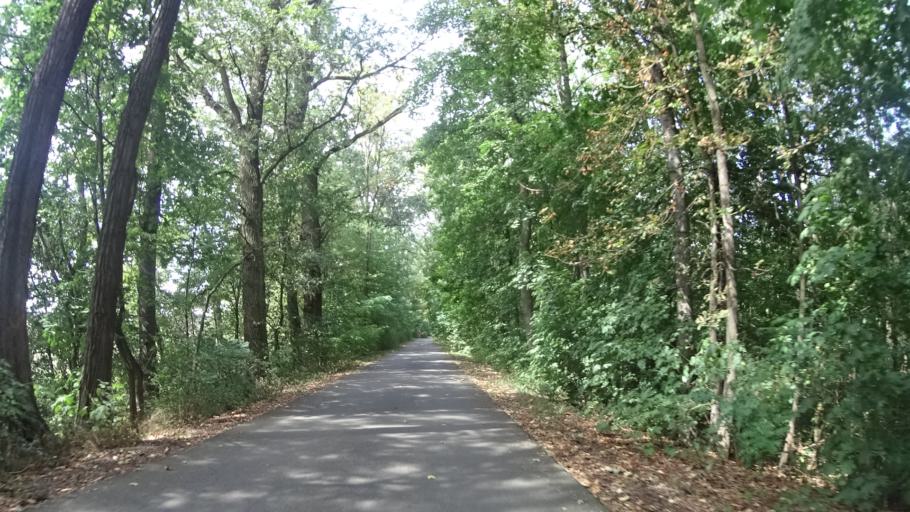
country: CZ
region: Olomoucky
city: Horka nad Moravou
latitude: 49.6482
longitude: 17.1963
